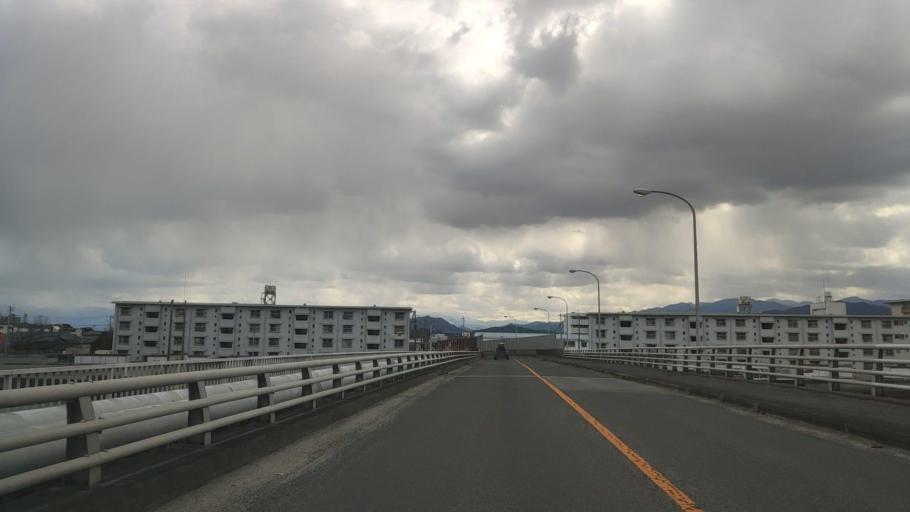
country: JP
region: Ehime
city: Saijo
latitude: 34.0596
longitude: 133.0175
